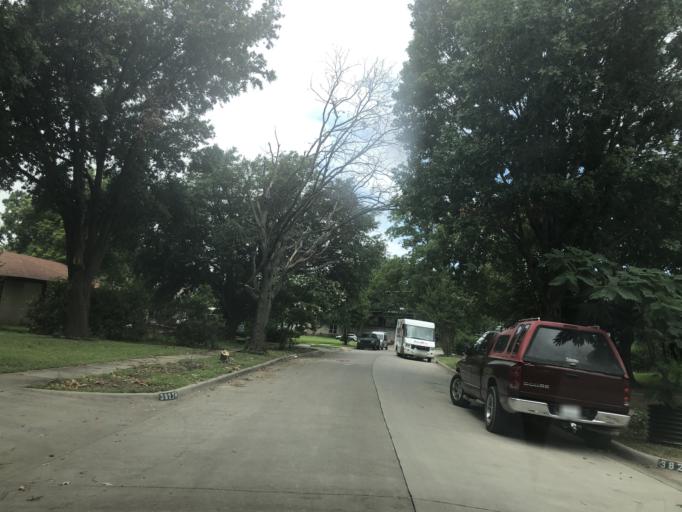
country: US
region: Texas
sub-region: Dallas County
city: University Park
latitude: 32.8636
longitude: -96.8518
